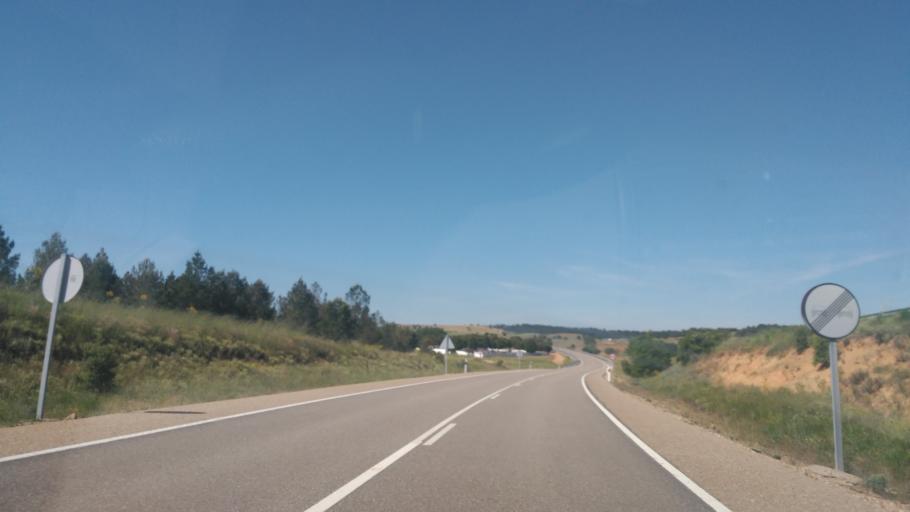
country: ES
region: Castille and Leon
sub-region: Provincia de Zamora
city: Cuelgamures
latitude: 41.2477
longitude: -5.7065
